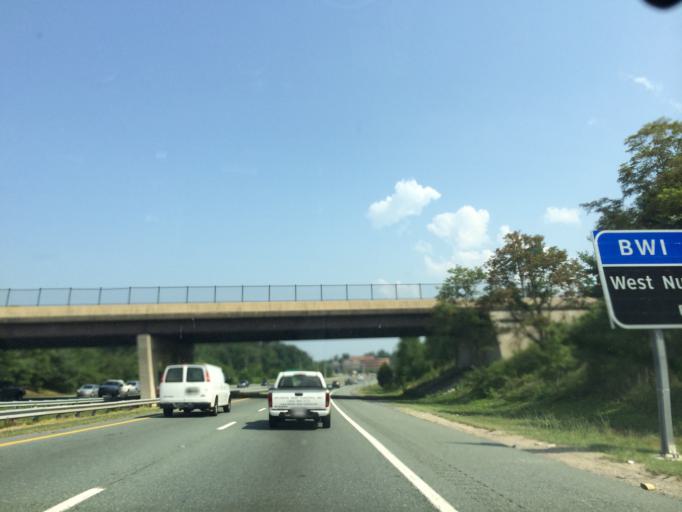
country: US
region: Maryland
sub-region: Howard County
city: Hanover
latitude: 39.1782
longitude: -76.7400
